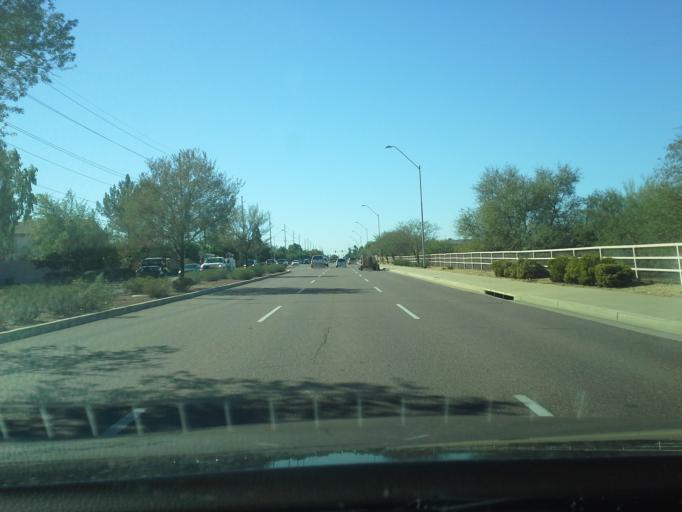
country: US
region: Arizona
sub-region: Maricopa County
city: Paradise Valley
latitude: 33.6406
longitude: -111.9705
